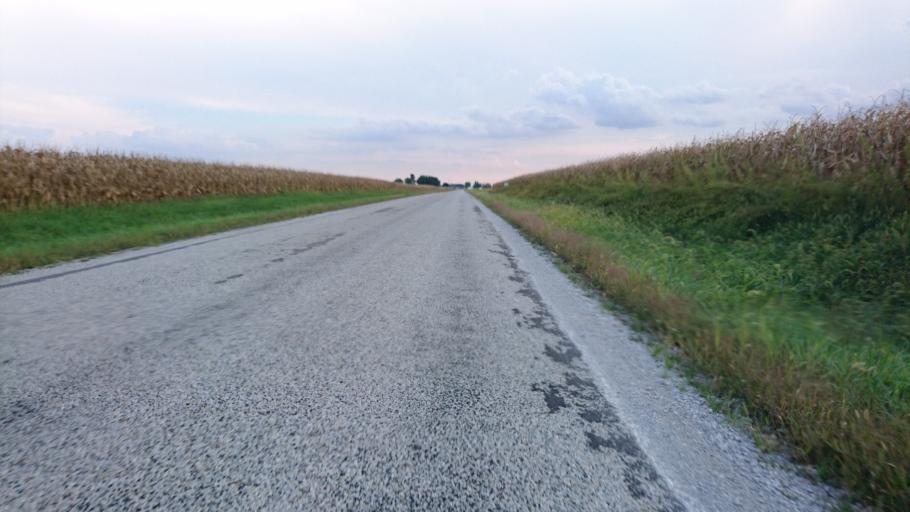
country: US
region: Illinois
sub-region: Logan County
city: Atlanta
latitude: 40.2499
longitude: -89.2051
